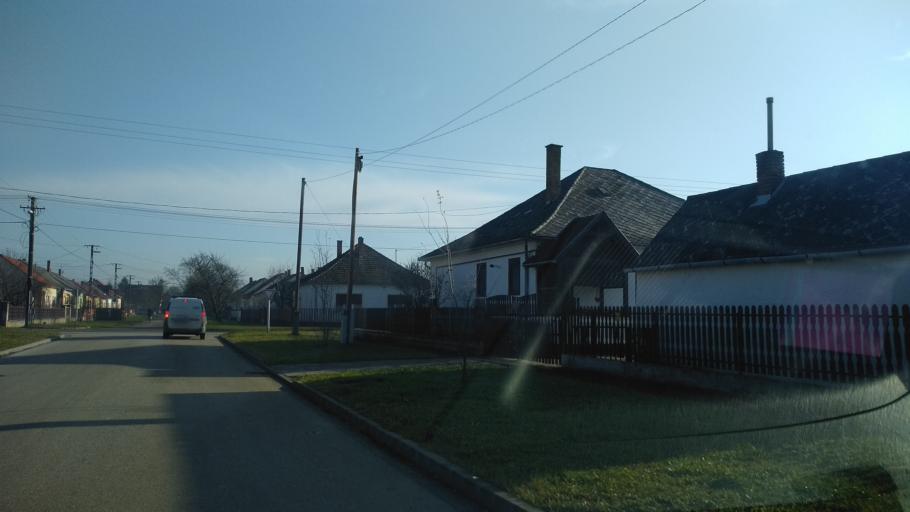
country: HU
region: Somogy
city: Barcs
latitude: 45.9649
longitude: 17.4547
